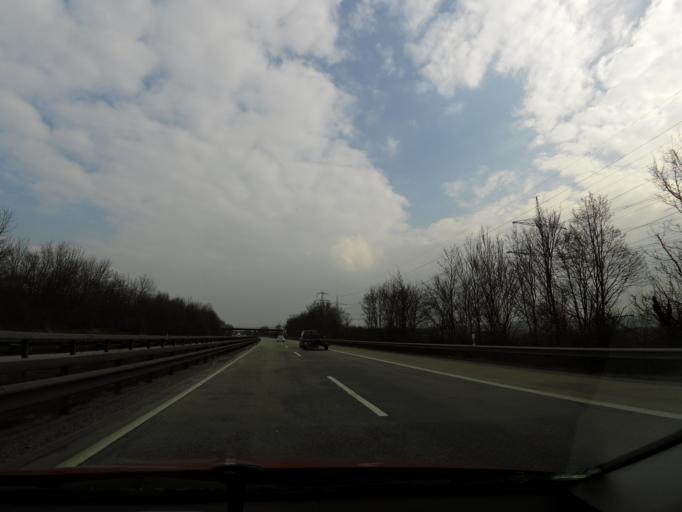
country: DE
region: Rheinland-Pfalz
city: Armsheim
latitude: 49.7992
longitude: 8.0598
